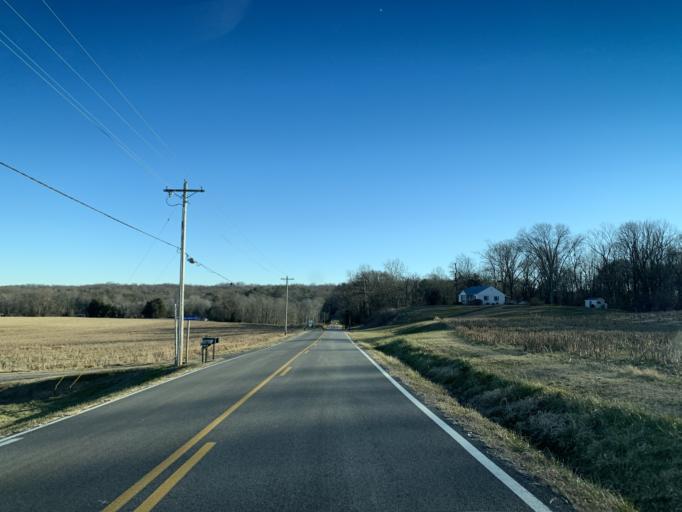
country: US
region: Maryland
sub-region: Saint Mary's County
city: Golden Beach
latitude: 38.4552
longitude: -76.6808
